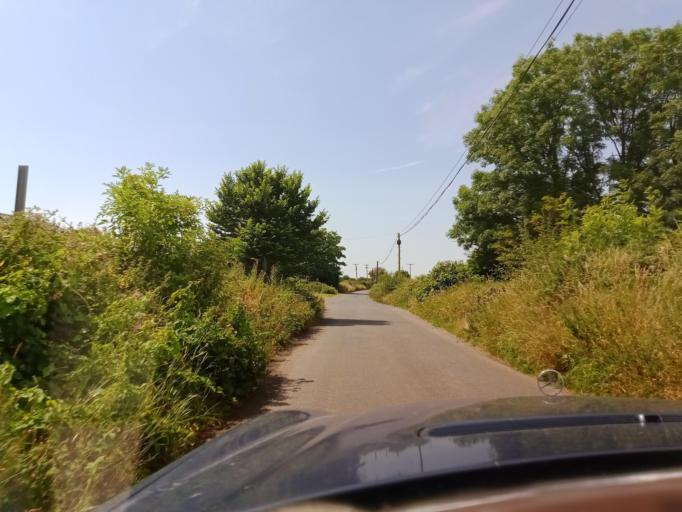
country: IE
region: Leinster
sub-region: Kilkenny
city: Mooncoin
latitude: 52.2744
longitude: -7.2193
